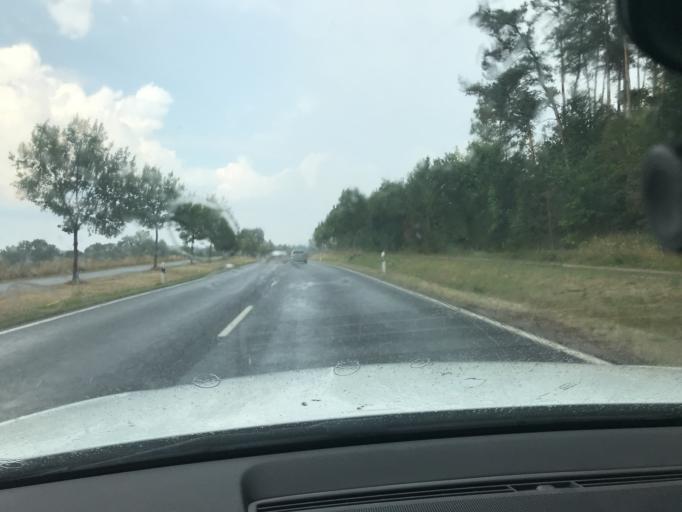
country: DE
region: Bavaria
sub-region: Upper Palatinate
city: Speinshart
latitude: 49.7540
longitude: 11.7908
